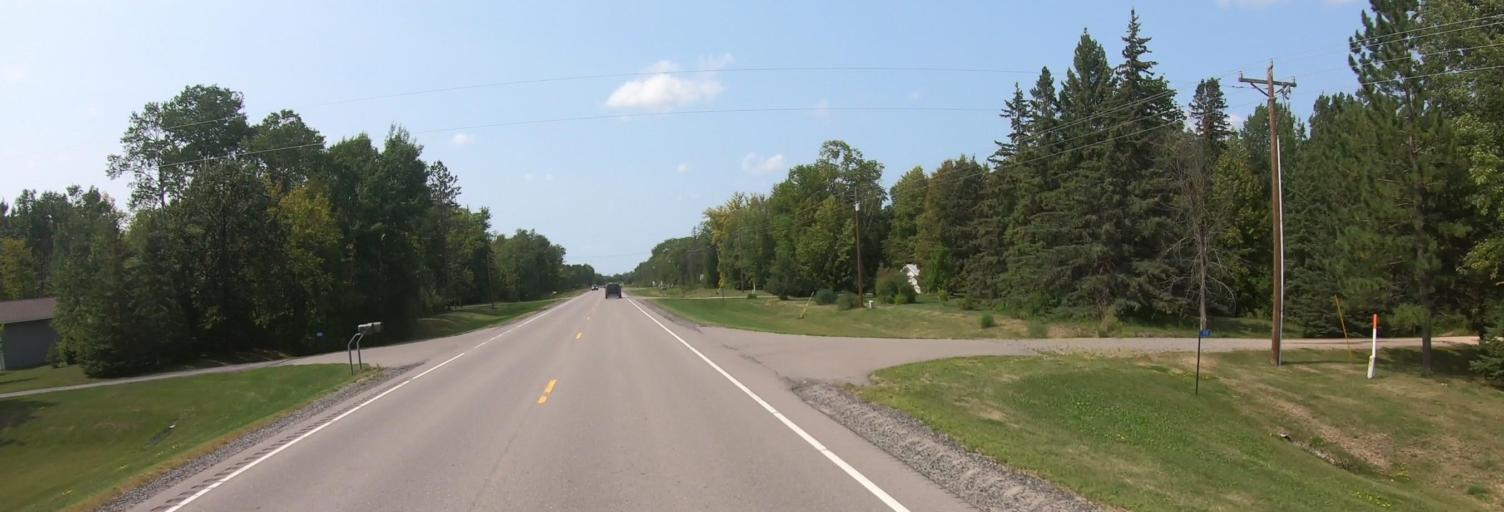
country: US
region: Minnesota
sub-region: Lake of the Woods County
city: Baudette
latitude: 48.6983
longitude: -94.5273
